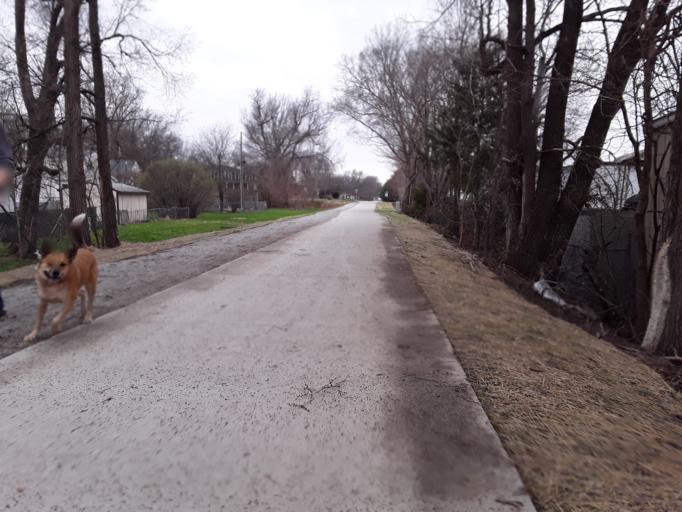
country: US
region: Nebraska
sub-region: Lancaster County
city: Lincoln
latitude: 40.8514
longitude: -96.6291
